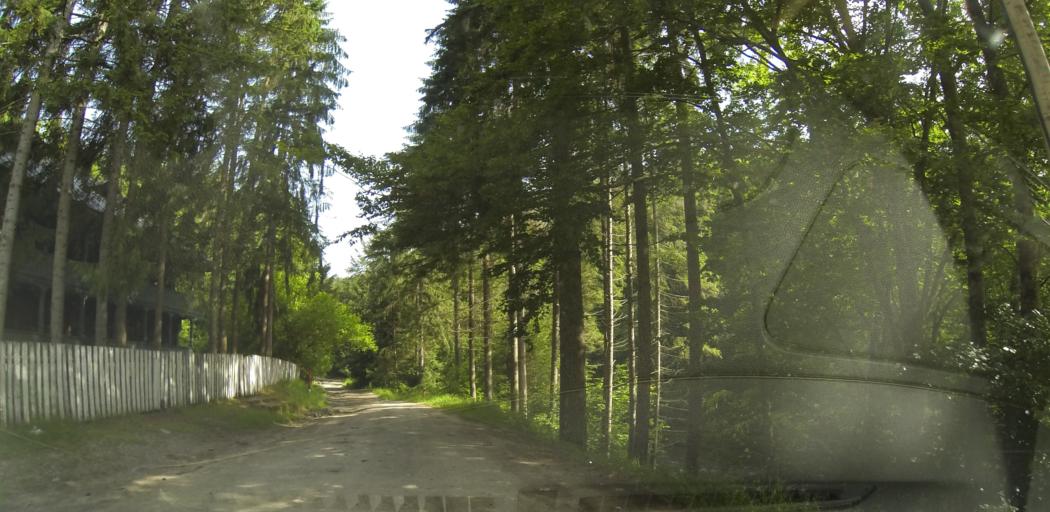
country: RO
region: Valcea
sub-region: Oras Baile Olanesti
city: Baile Olanesti
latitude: 45.2222
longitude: 24.2113
